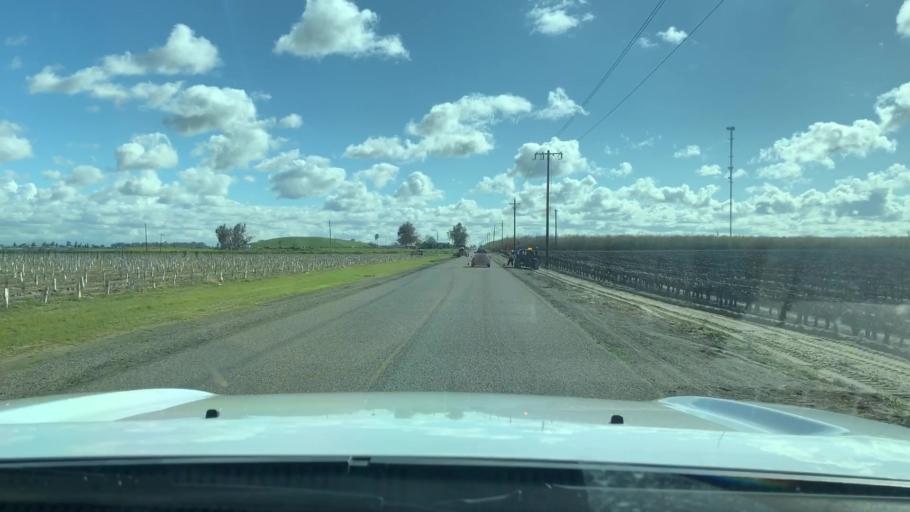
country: US
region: California
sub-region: Fresno County
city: Caruthers
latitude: 36.5474
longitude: -119.7581
